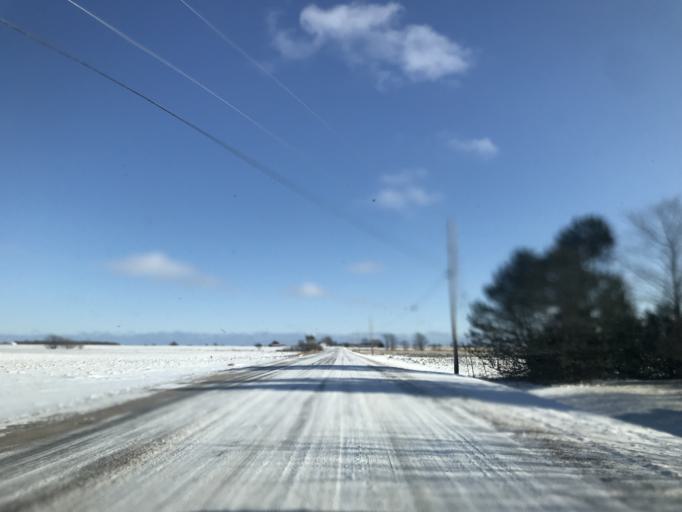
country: US
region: Wisconsin
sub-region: Kewaunee County
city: Luxemburg
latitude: 44.6976
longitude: -87.6098
